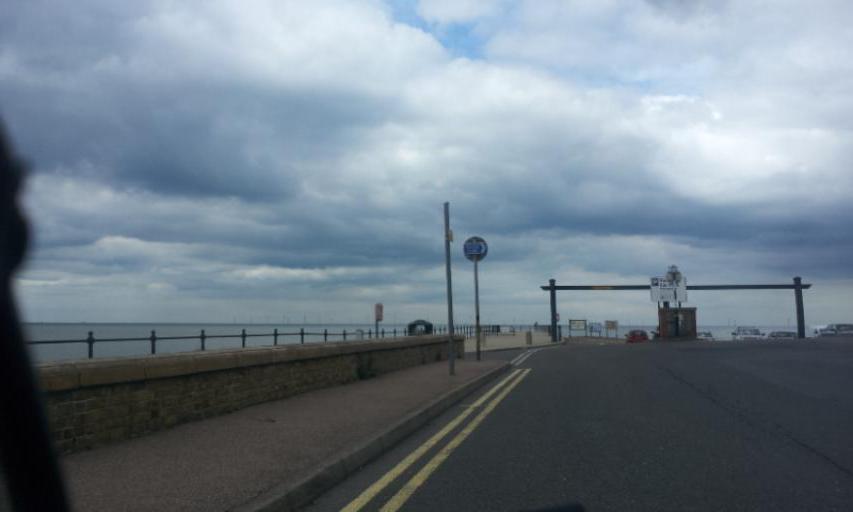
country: GB
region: England
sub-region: Kent
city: Herne Bay
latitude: 51.3719
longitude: 1.0989
